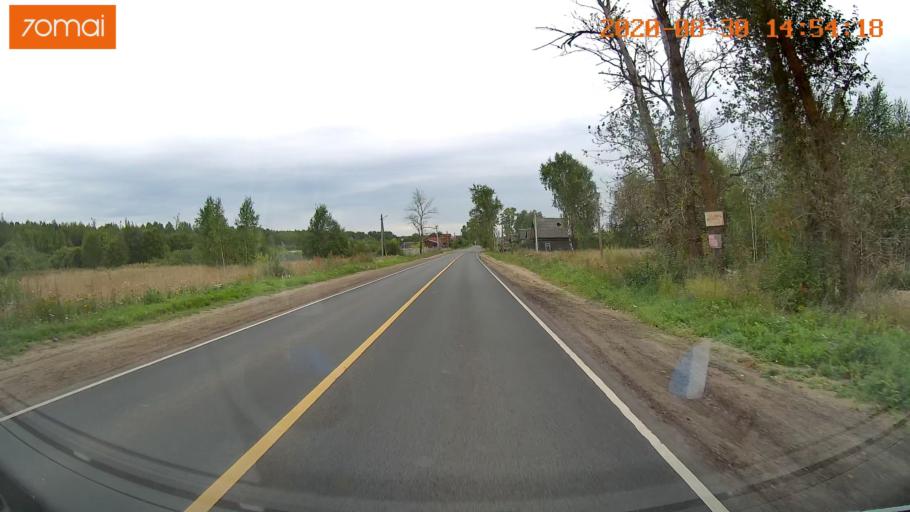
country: RU
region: Ivanovo
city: Kineshma
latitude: 57.3948
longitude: 42.0460
